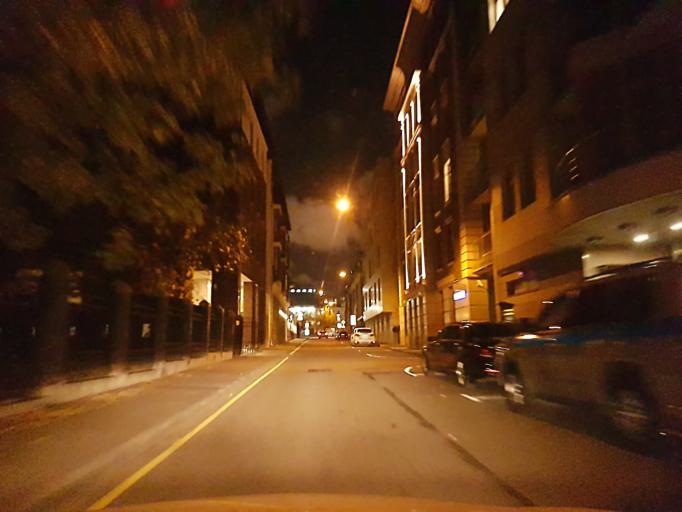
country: RU
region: Moscow
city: Moscow
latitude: 55.7404
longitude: 37.6017
